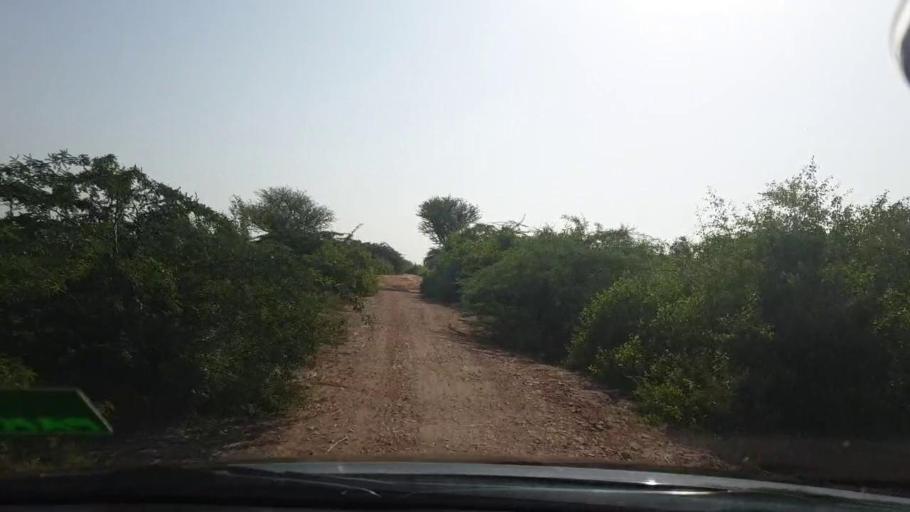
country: PK
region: Sindh
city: Tando Bago
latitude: 24.7126
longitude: 68.9817
